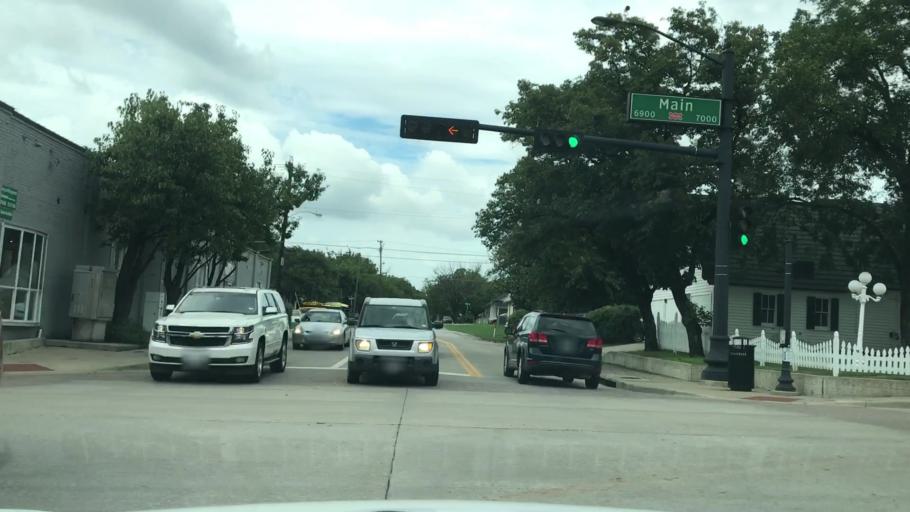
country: US
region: Texas
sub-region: Collin County
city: Frisco
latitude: 33.1504
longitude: -96.8239
